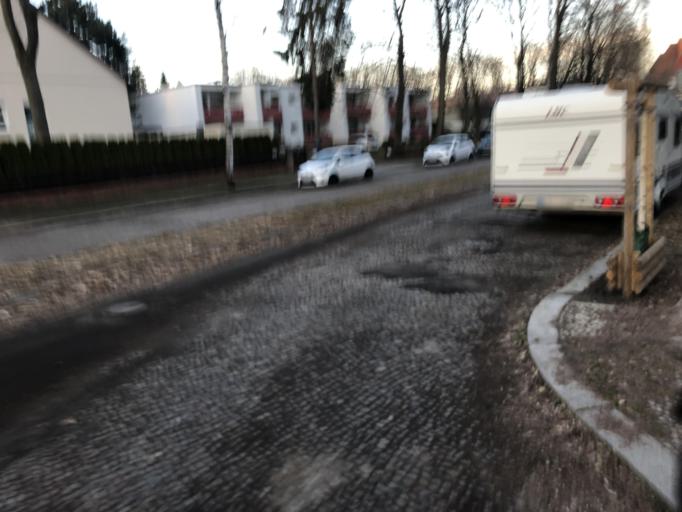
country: DE
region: Berlin
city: Frohnau
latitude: 52.6448
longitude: 13.2865
